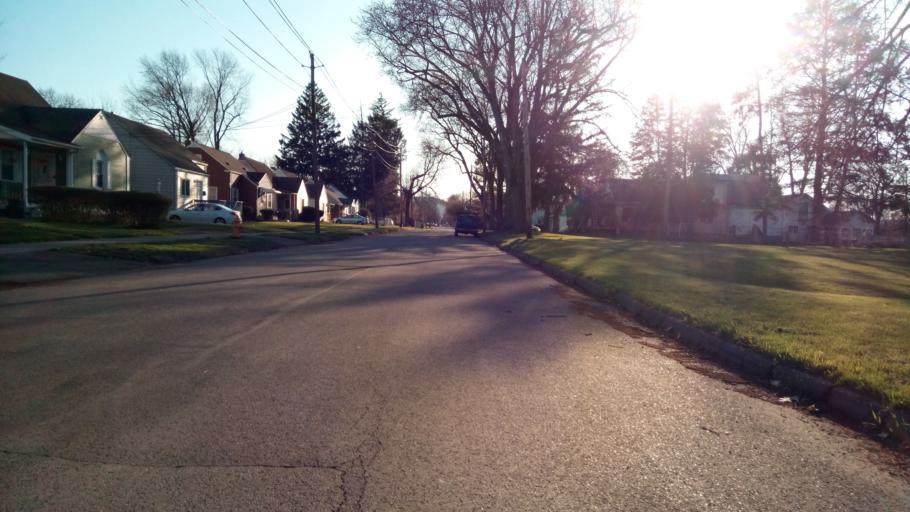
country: US
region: New York
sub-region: Chemung County
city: Elmira
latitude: 42.0810
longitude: -76.7847
